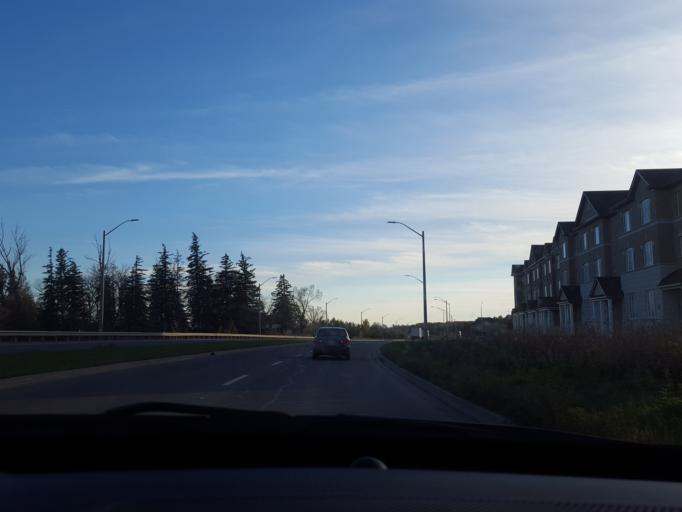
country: CA
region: Ontario
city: Markham
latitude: 43.8905
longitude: -79.2130
